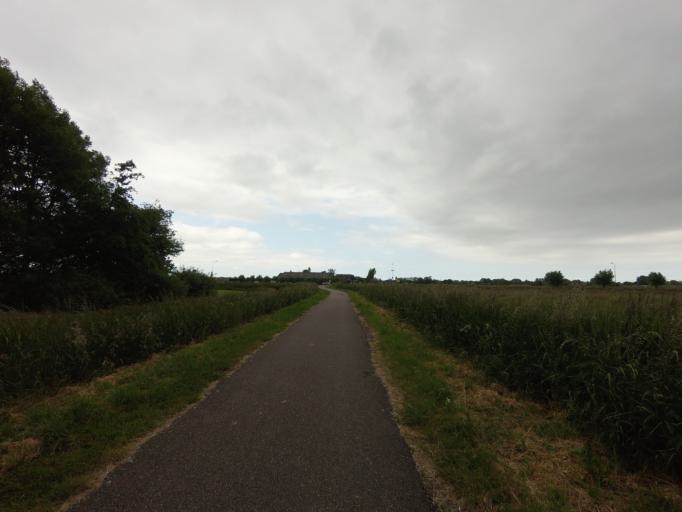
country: NL
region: North Holland
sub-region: Gemeente Hoorn
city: Hoorn
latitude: 52.6697
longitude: 5.0203
